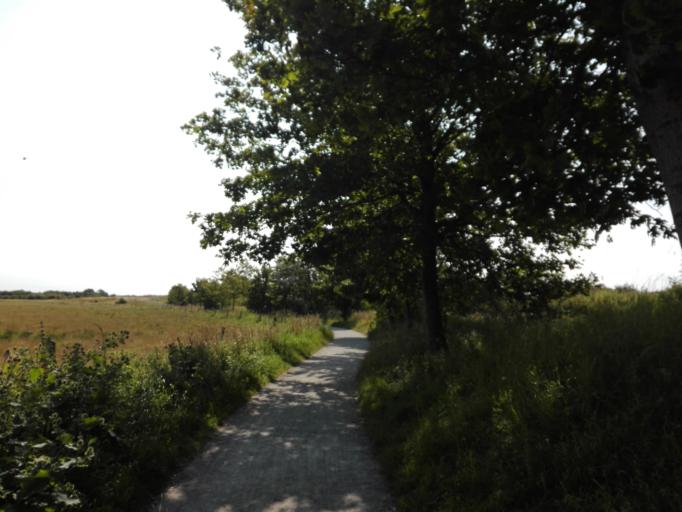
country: DK
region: Central Jutland
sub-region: Arhus Kommune
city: Lystrup
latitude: 56.2145
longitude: 10.2108
